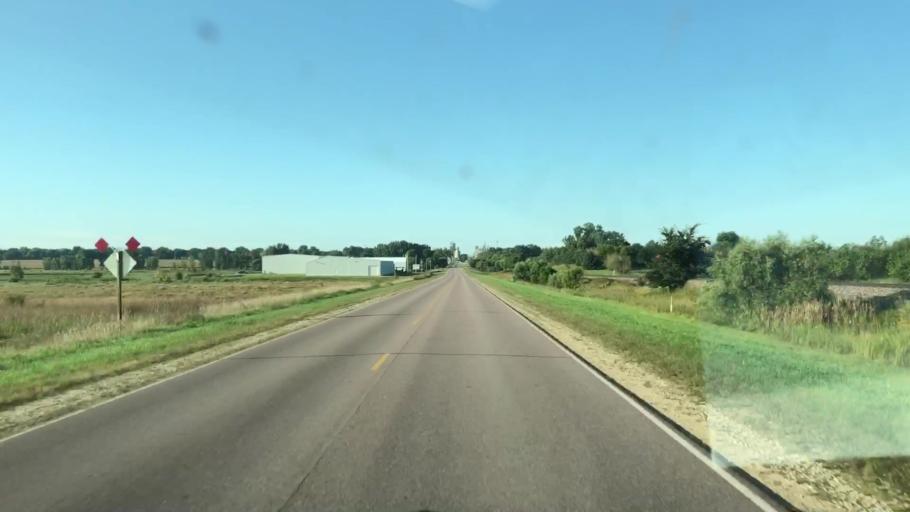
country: US
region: Iowa
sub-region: O'Brien County
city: Sheldon
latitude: 43.2025
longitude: -95.8455
